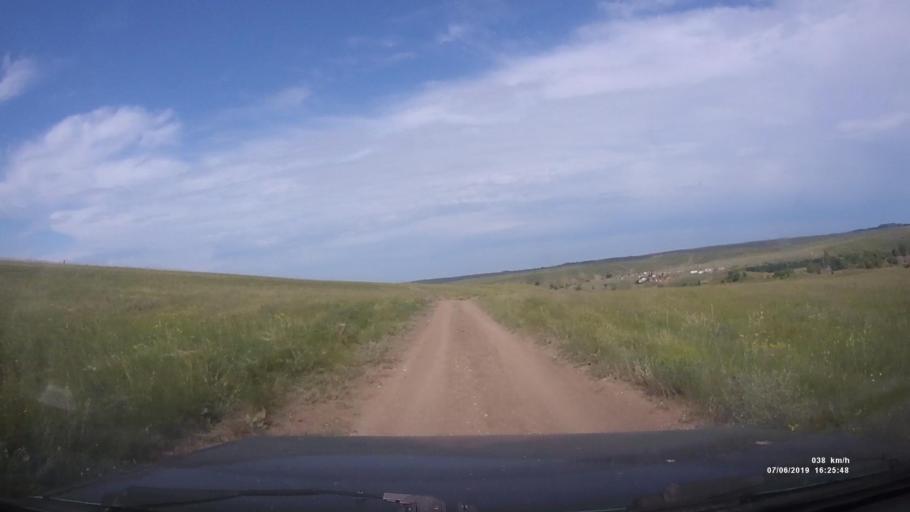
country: RU
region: Rostov
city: Kamensk-Shakhtinskiy
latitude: 48.2537
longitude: 40.3095
